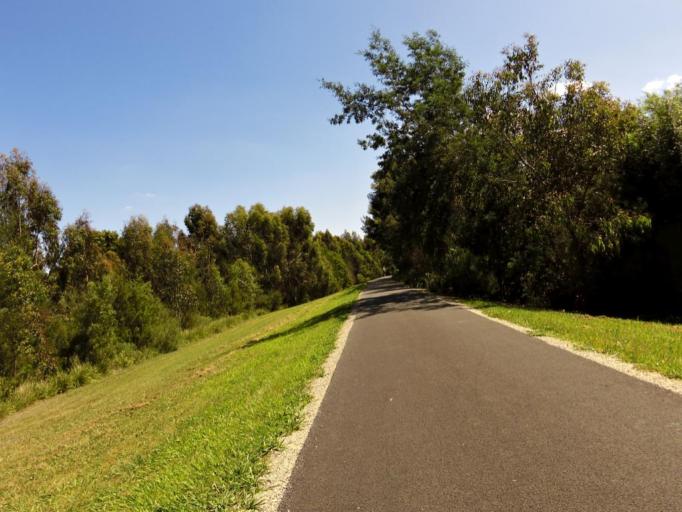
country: AU
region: Victoria
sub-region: Knox
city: Knoxfield
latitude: -37.8998
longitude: 145.2652
